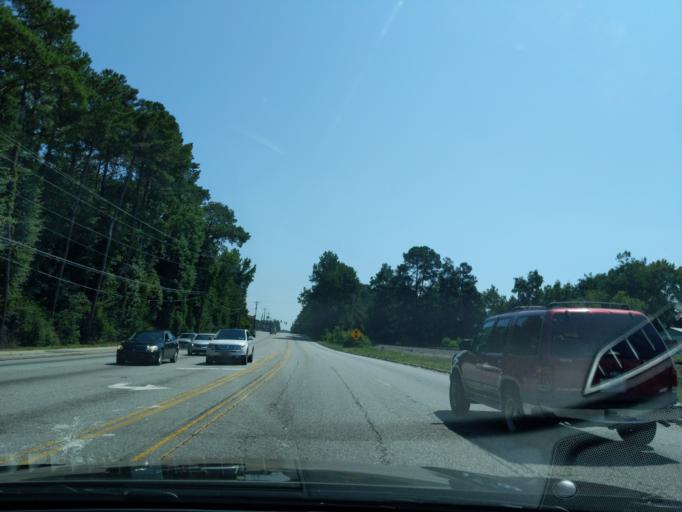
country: US
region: South Carolina
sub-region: Lexington County
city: Oak Grove
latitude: 33.9721
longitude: -81.1376
